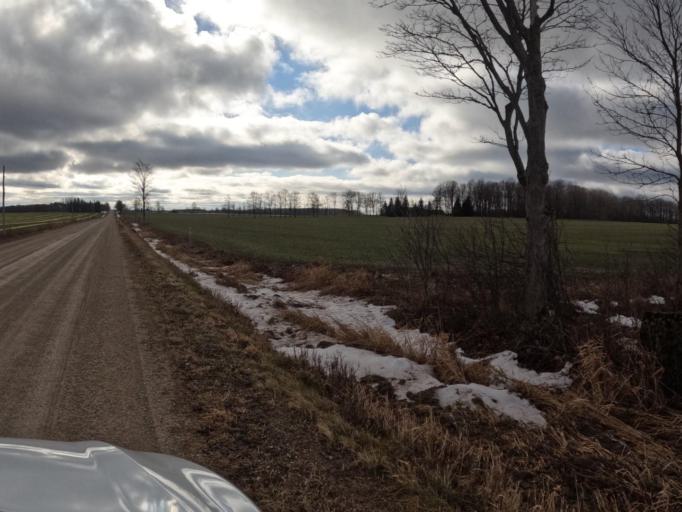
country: CA
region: Ontario
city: Shelburne
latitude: 43.9805
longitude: -80.3821
